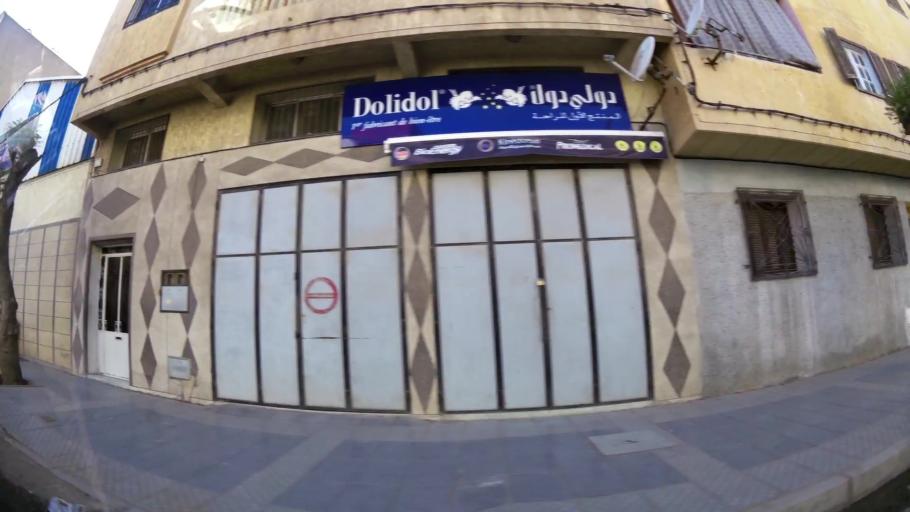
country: MA
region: Oriental
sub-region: Oujda-Angad
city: Oujda
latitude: 34.6770
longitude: -1.9086
